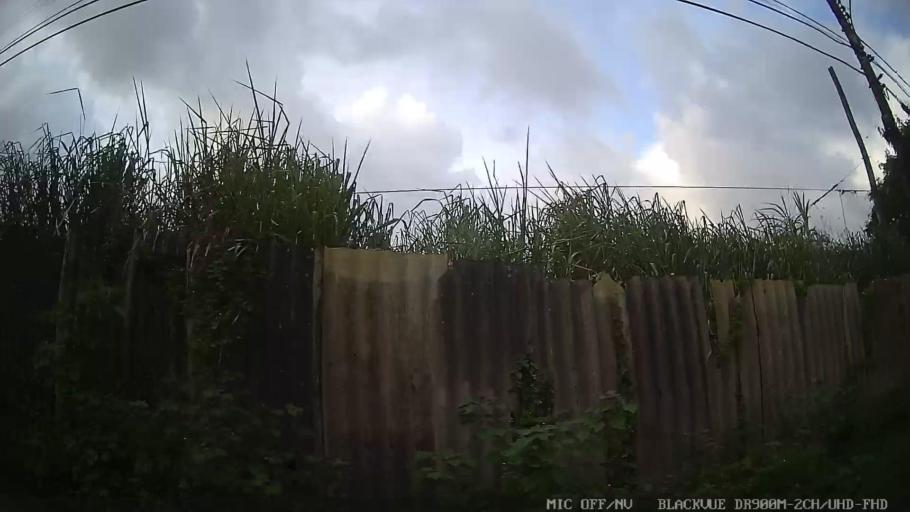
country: BR
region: Sao Paulo
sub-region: Itanhaem
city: Itanhaem
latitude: -24.1723
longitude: -46.7728
